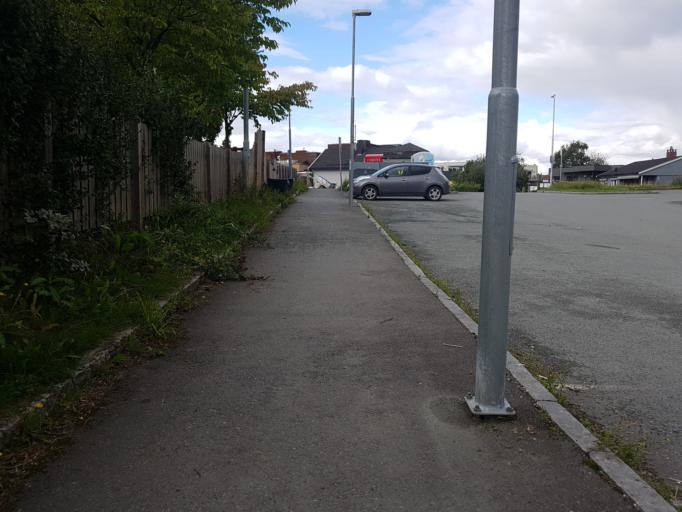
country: NO
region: Sor-Trondelag
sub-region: Trondheim
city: Trondheim
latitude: 63.4288
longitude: 10.4618
